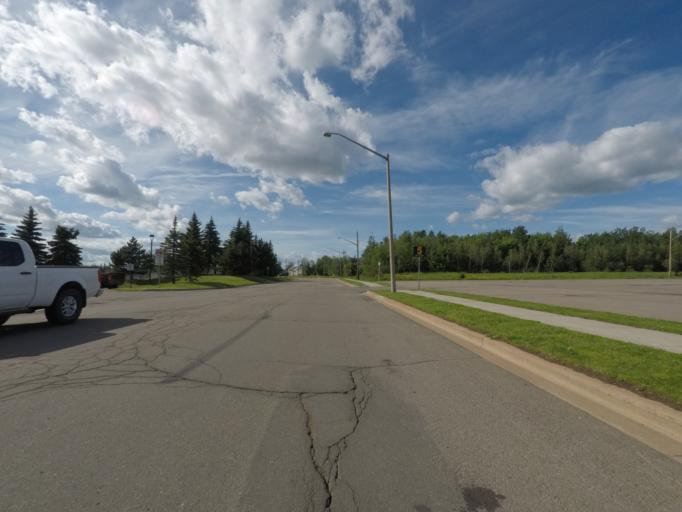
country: CA
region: New Brunswick
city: Moncton
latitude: 46.0963
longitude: -64.8331
